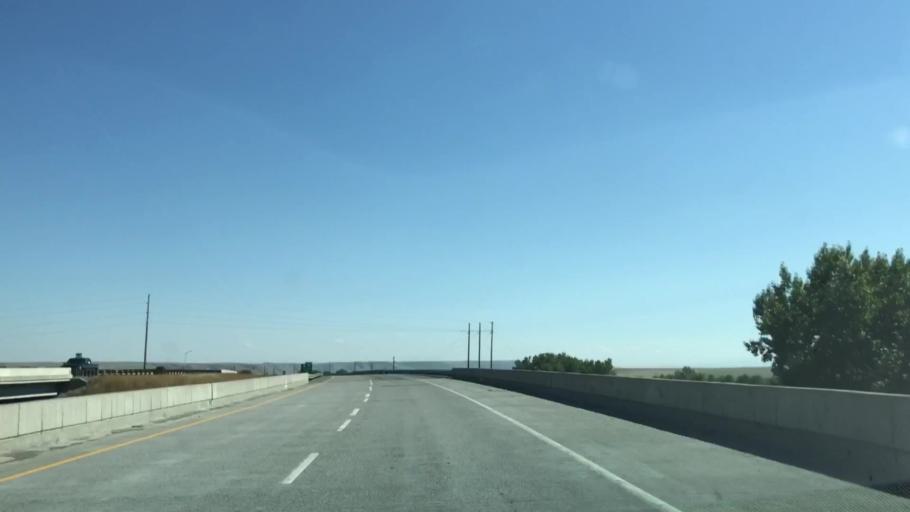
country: US
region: Montana
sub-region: Gallatin County
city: Three Forks
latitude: 45.9054
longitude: -111.5436
